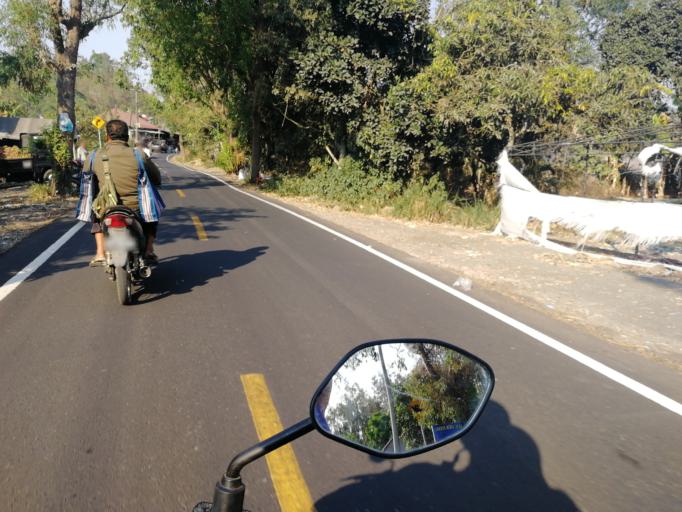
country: ID
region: Bali
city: Banjar Trunyan
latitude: -8.2422
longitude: 115.4028
